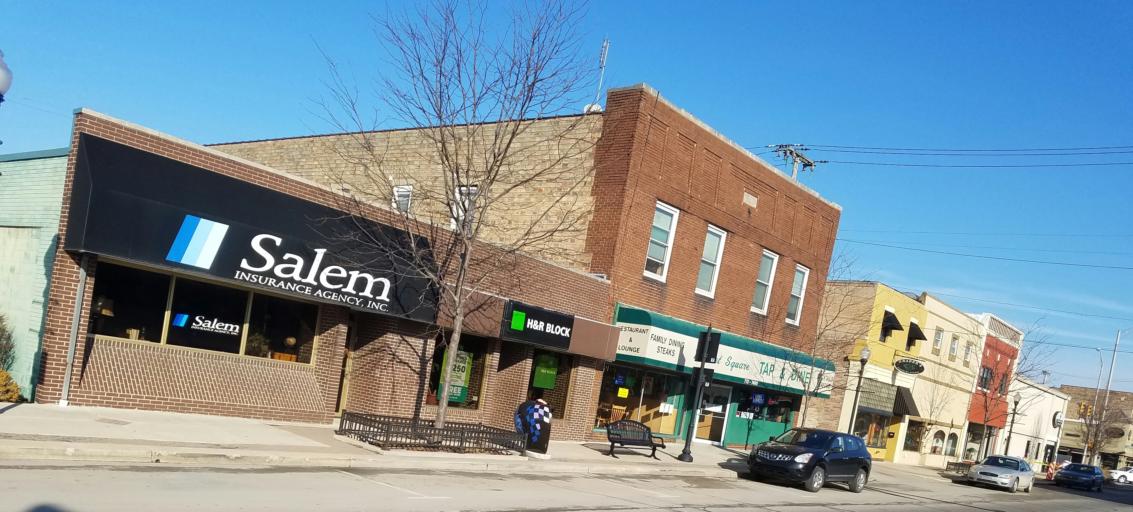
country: US
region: Indiana
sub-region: Elkhart County
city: Nappanee
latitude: 41.4428
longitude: -86.0026
